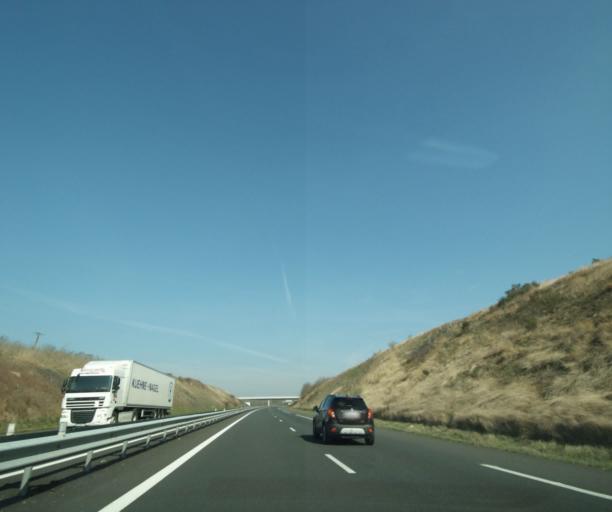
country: FR
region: Midi-Pyrenees
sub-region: Departement du Lot
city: Cahors
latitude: 44.5608
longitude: 1.5145
